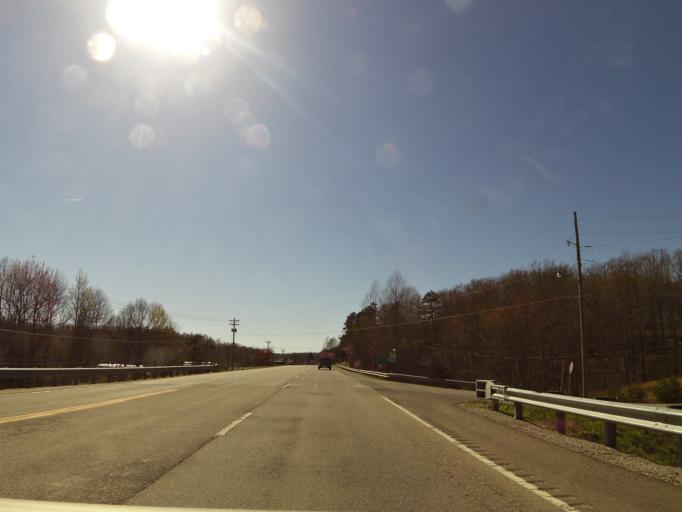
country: US
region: Tennessee
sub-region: Scott County
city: Oneida
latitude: 36.5380
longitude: -84.4651
